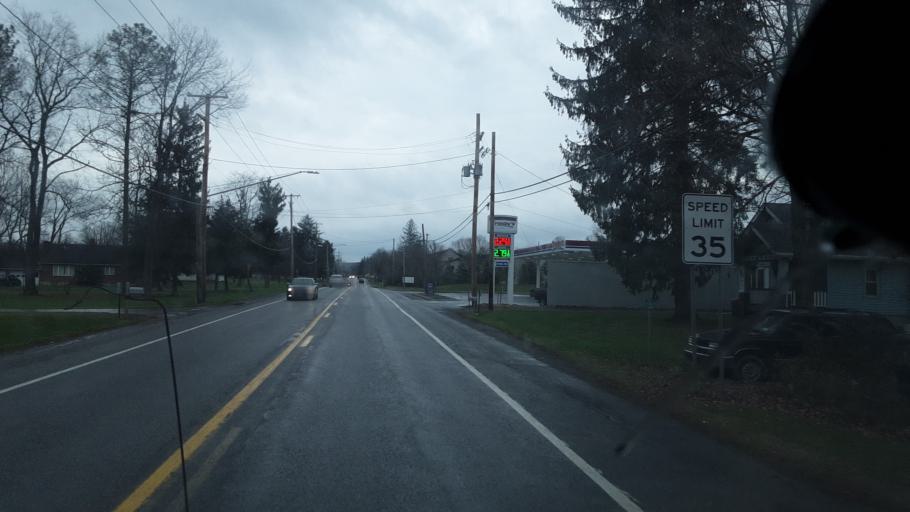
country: US
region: New York
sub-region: Erie County
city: Holland
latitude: 42.6575
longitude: -78.5536
